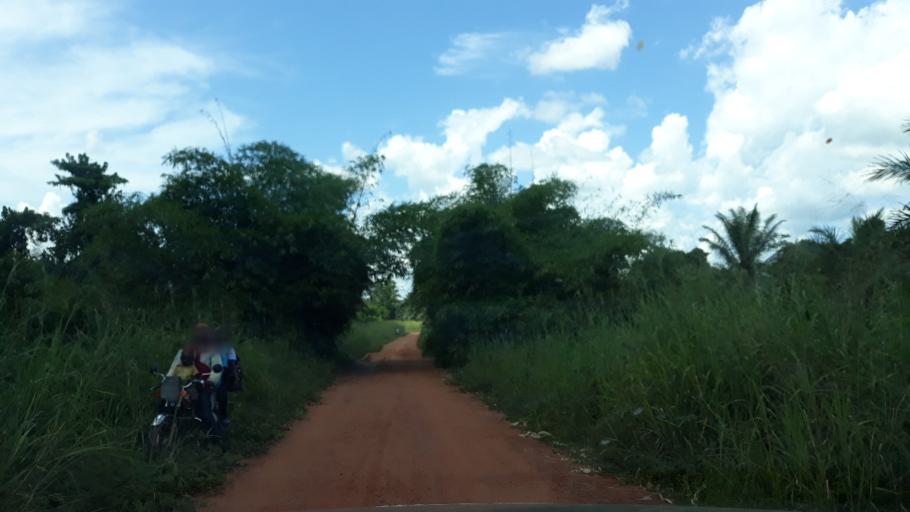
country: CD
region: Equateur
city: Businga
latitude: 3.4037
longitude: 20.3832
